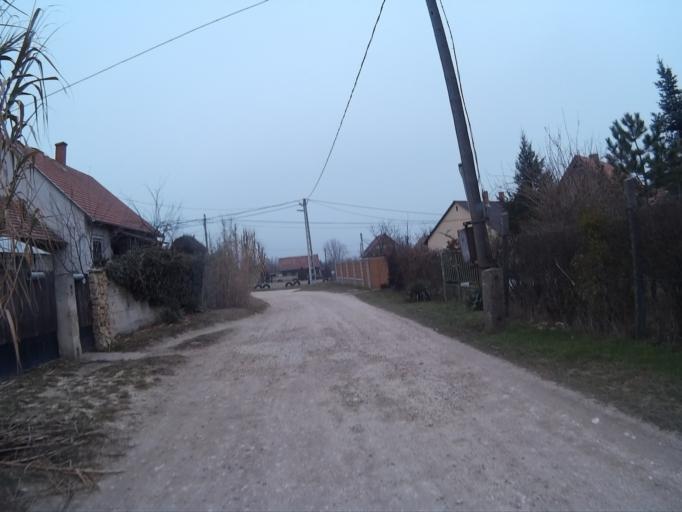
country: HU
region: Fejer
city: Csakvar
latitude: 47.3850
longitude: 18.4491
